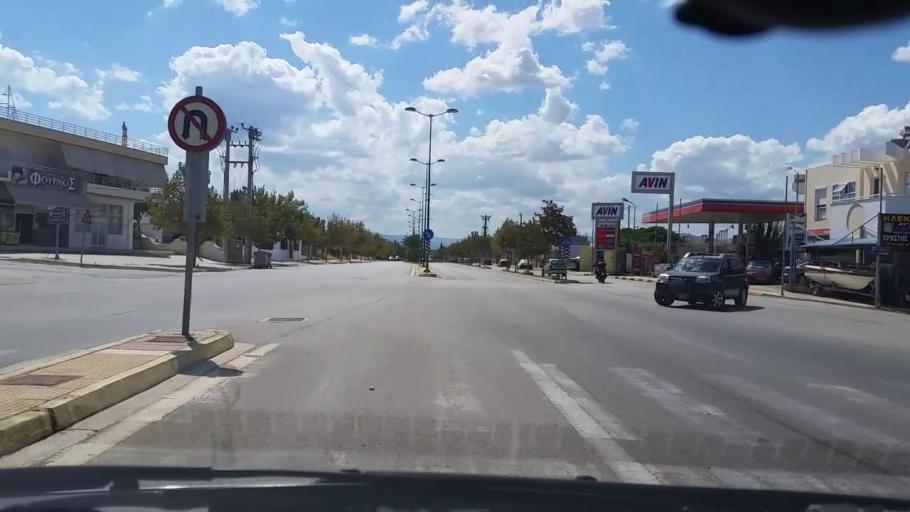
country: GR
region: Peloponnese
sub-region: Nomos Korinthias
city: Loutraki
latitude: 37.9647
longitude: 22.9785
